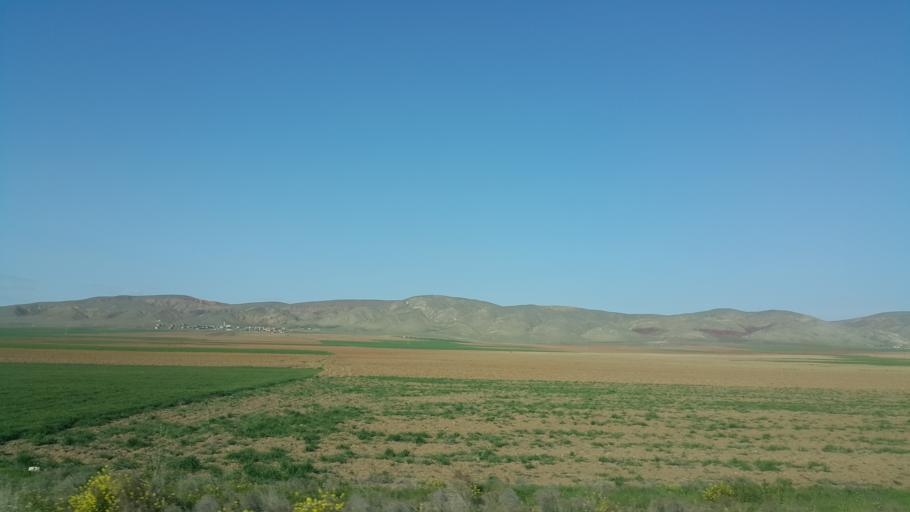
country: TR
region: Aksaray
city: Acipinar
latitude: 38.6521
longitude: 33.7235
